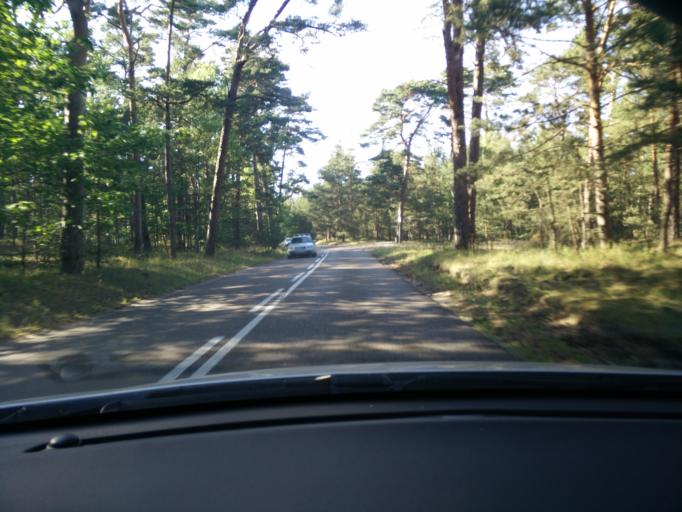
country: PL
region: Pomeranian Voivodeship
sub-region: Powiat pucki
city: Jastarnia
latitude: 54.6644
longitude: 18.7457
